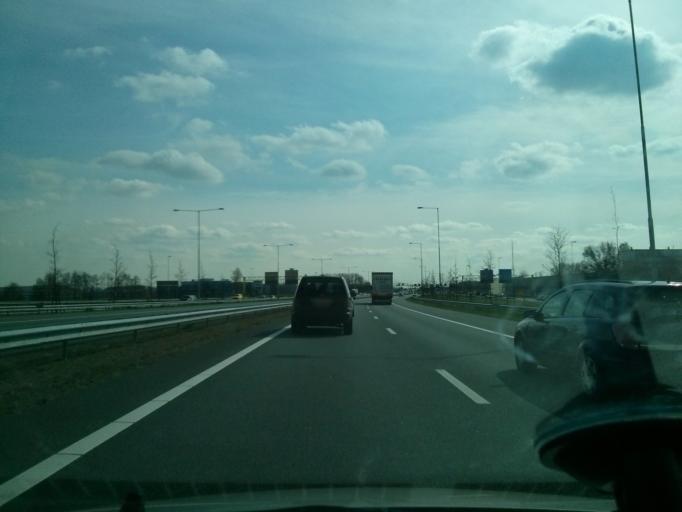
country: NL
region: North Brabant
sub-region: Gemeente 's-Hertogenbosch
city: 's-Hertogenbosch
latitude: 51.6968
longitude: 5.3519
